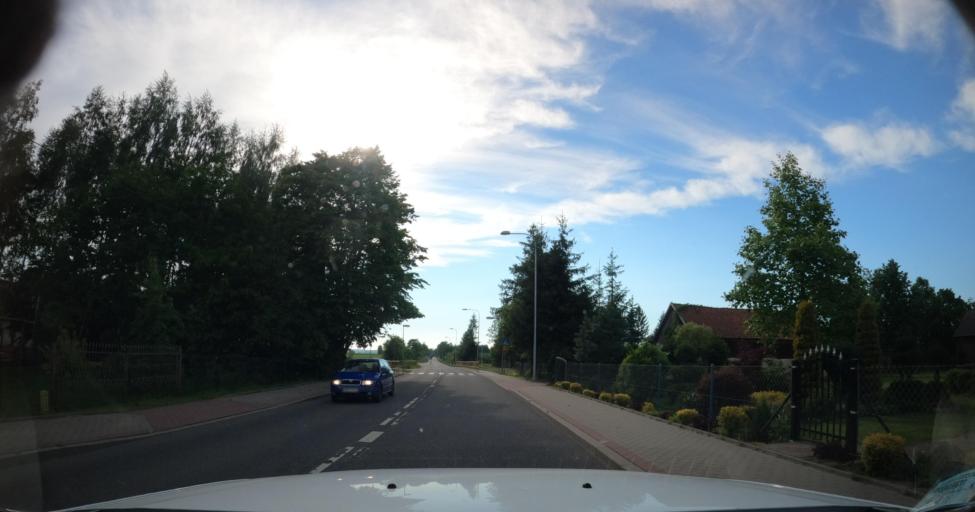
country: PL
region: Warmian-Masurian Voivodeship
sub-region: Powiat ostrodzki
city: Morag
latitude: 54.0812
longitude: 19.8985
